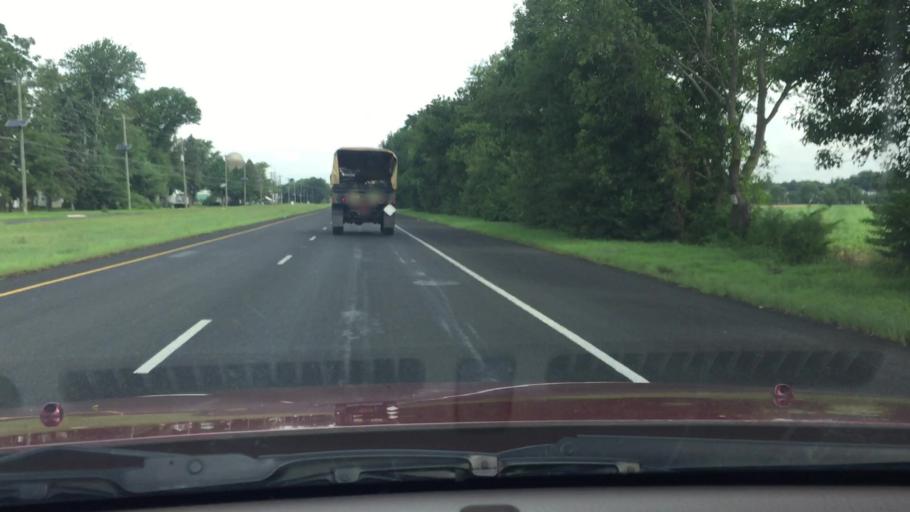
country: US
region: New Jersey
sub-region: Burlington County
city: Bordentown
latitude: 40.0939
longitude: -74.6817
